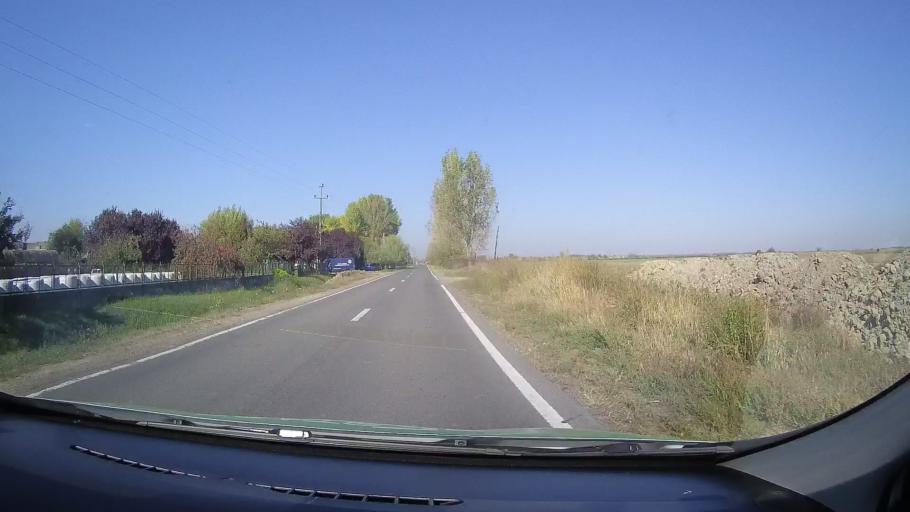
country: RO
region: Satu Mare
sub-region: Comuna Urziceni
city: Urziceni
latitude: 47.7217
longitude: 22.4151
